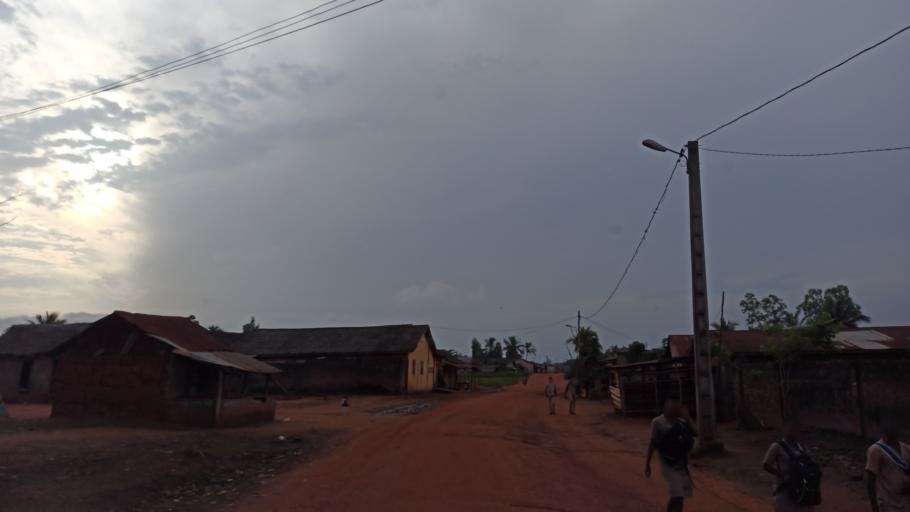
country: BJ
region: Queme
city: Porto-Novo
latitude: 6.5032
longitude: 2.6962
